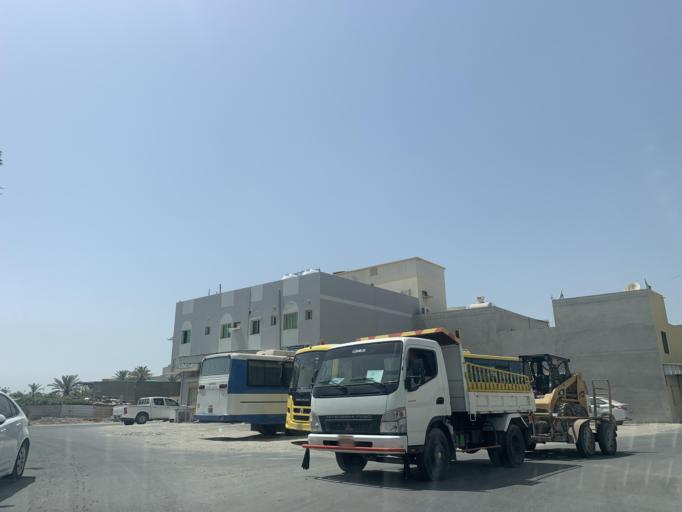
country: BH
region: Central Governorate
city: Madinat Hamad
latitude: 26.1507
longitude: 50.4986
